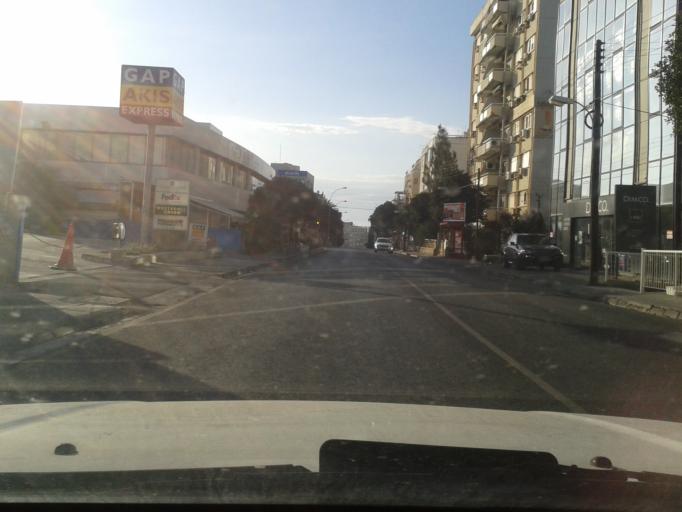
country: CY
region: Lefkosia
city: Nicosia
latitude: 35.1581
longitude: 33.3653
